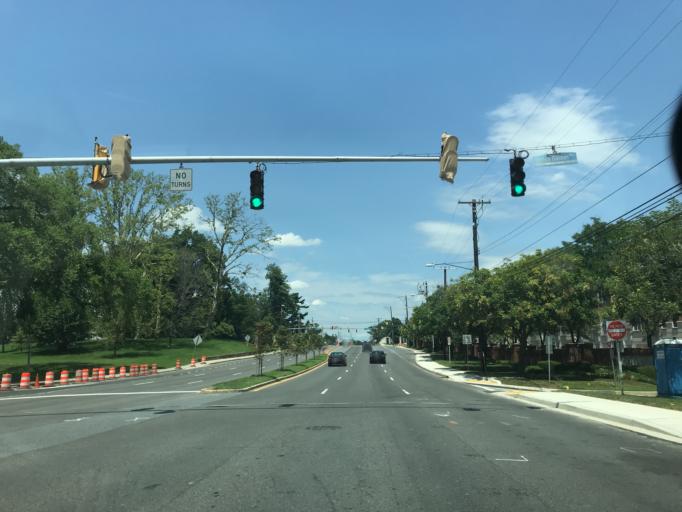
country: US
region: Maryland
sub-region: Montgomery County
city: Bethesda
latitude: 38.9951
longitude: -77.0964
